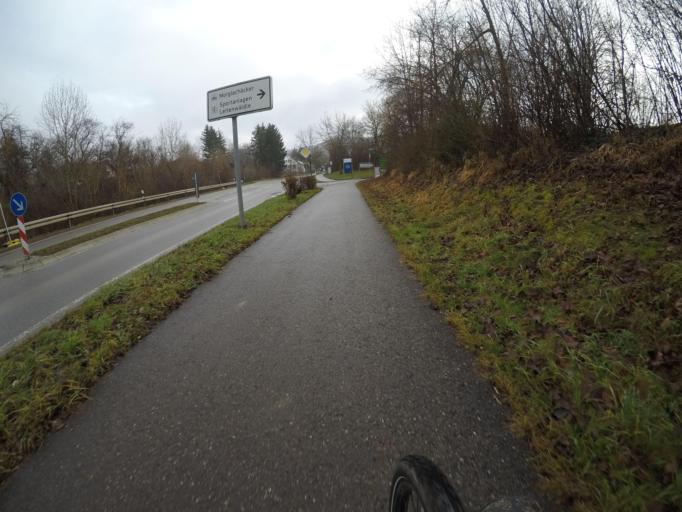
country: DE
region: Baden-Wuerttemberg
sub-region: Regierungsbezirk Stuttgart
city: Beuren
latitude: 48.5748
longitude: 9.3925
